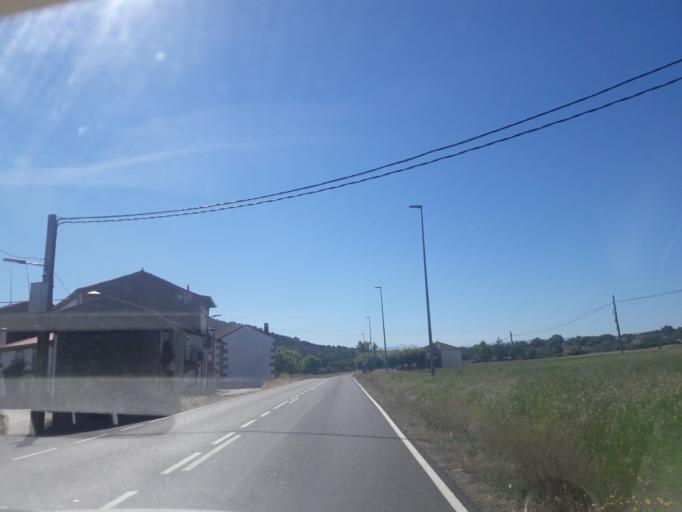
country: ES
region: Castille and Leon
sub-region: Provincia de Salamanca
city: Nava de Bejar
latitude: 40.4952
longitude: -5.6646
